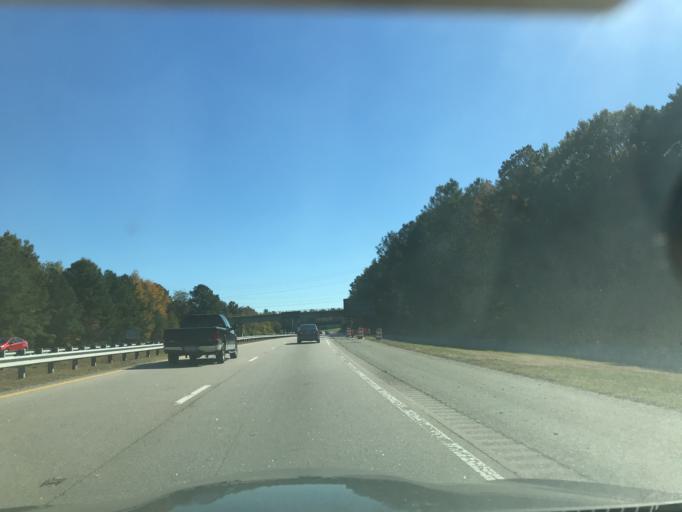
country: US
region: North Carolina
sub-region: Durham County
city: Durham
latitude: 36.0123
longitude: -78.9349
